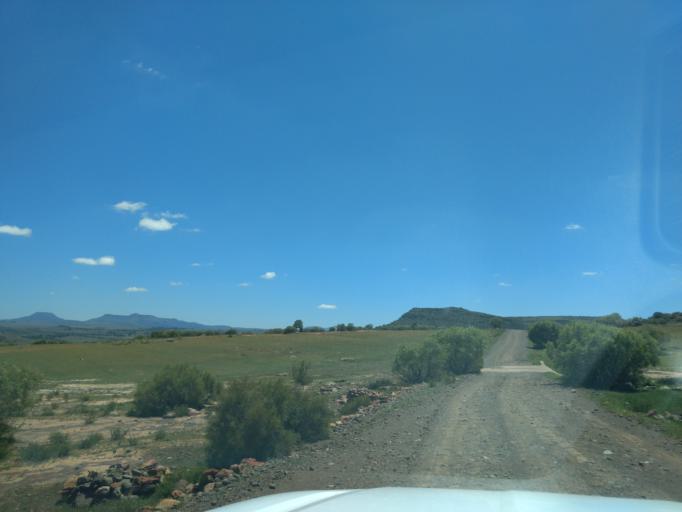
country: LS
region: Maseru
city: Maseru
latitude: -29.4568
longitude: 27.3680
